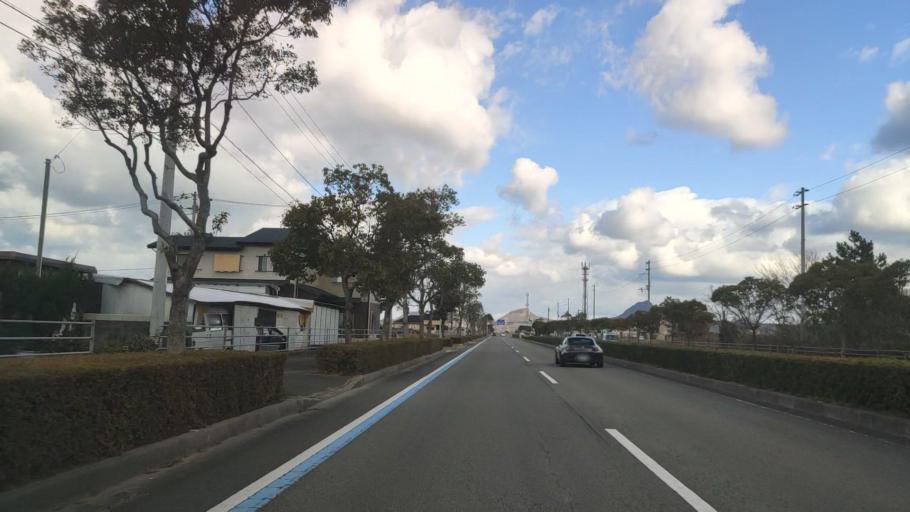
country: JP
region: Ehime
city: Hojo
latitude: 33.9507
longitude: 132.7744
